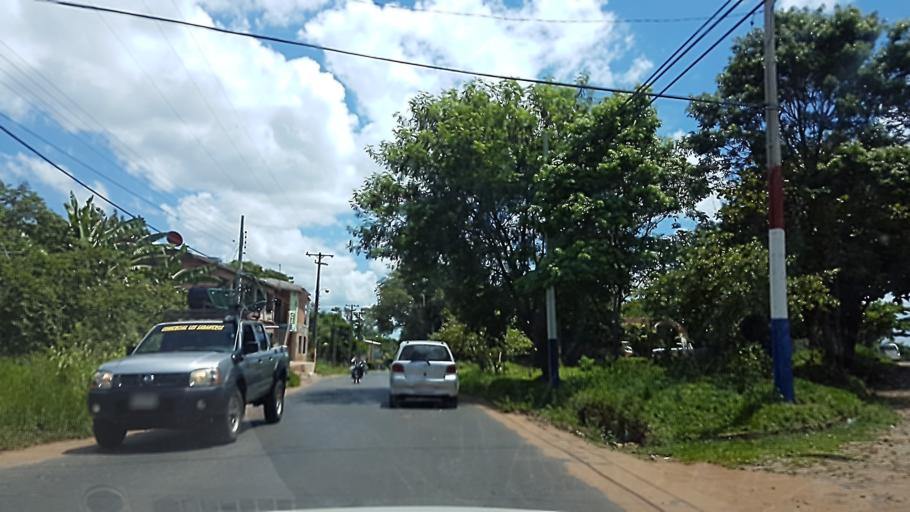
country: PY
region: Central
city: San Lorenzo
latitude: -25.2839
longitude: -57.4948
